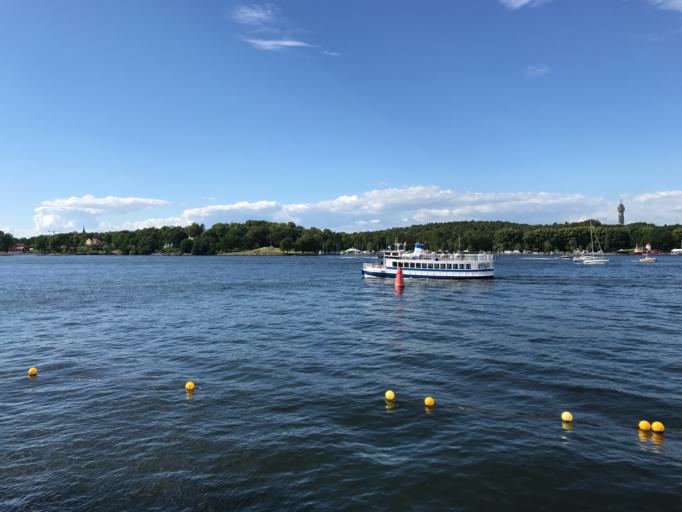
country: SE
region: Stockholm
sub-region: Nacka Kommun
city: Nacka
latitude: 59.3164
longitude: 18.1280
